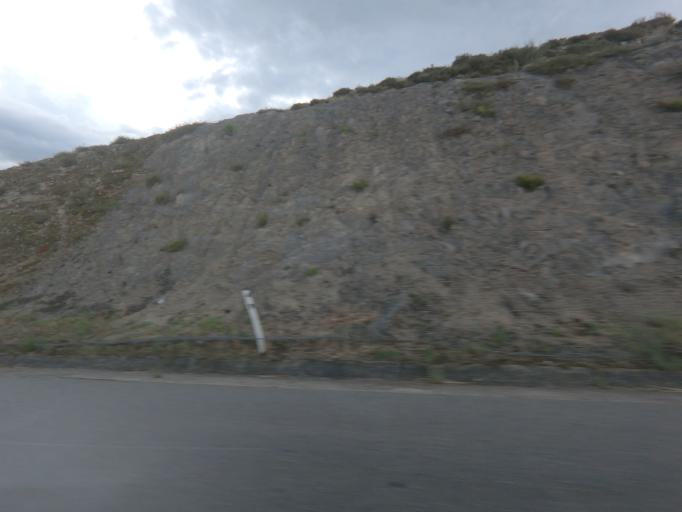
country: PT
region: Viseu
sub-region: Lamego
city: Lamego
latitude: 41.0402
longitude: -7.8593
